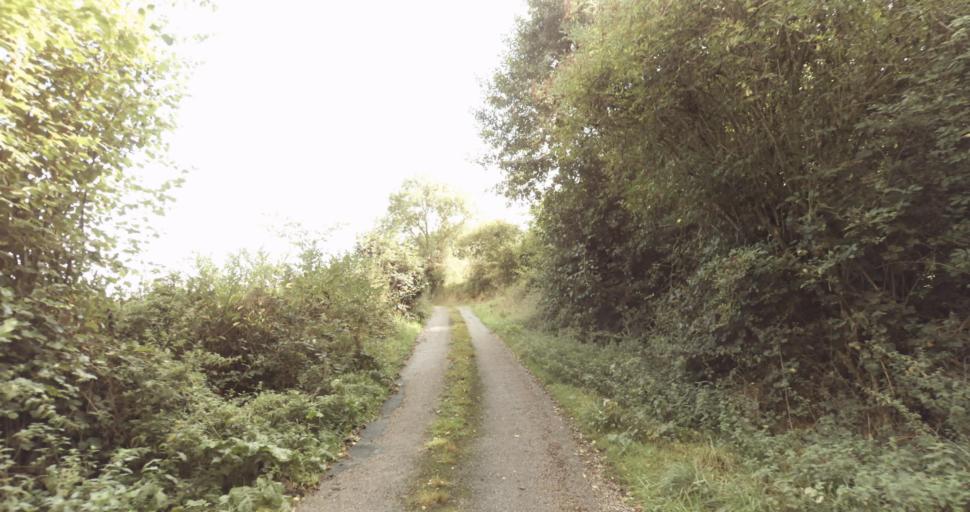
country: FR
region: Lower Normandy
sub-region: Departement de l'Orne
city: Vimoutiers
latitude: 48.8816
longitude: 0.1757
